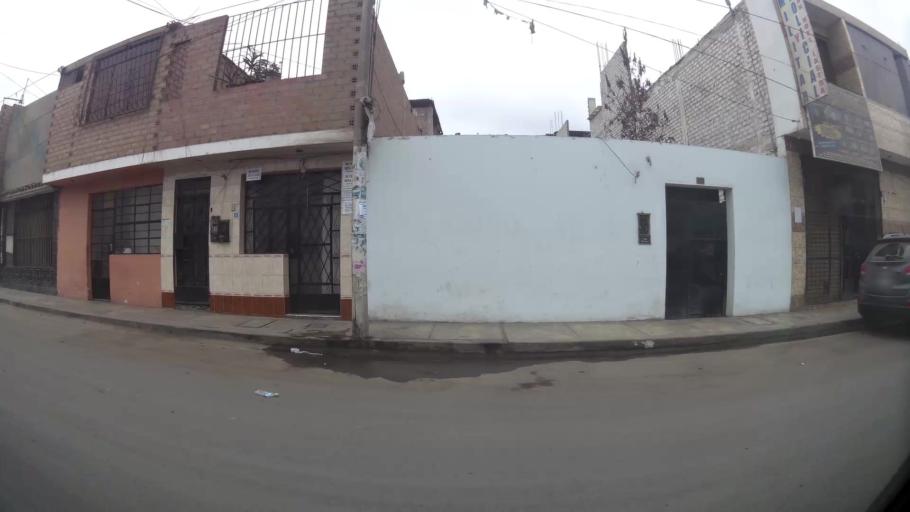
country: PE
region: Lima
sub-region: Provincia de Huaral
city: Huaral
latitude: -11.4895
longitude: -77.2063
